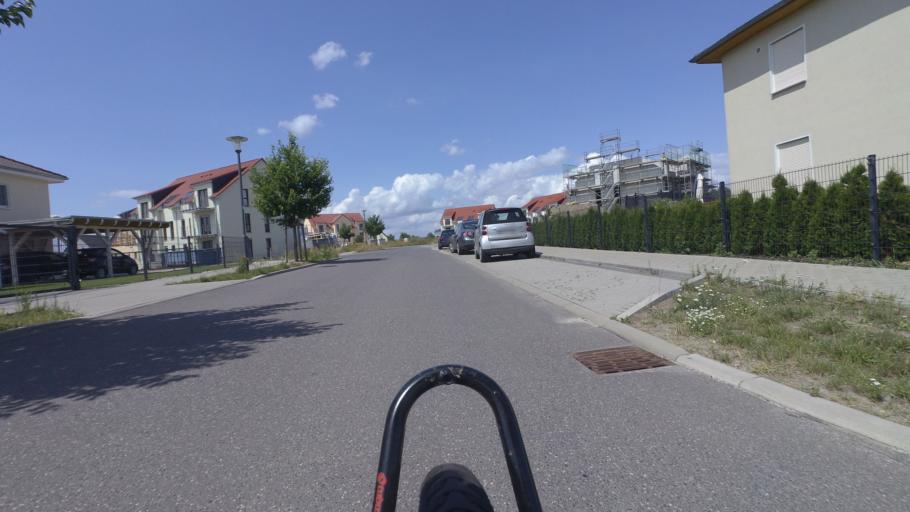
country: DE
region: Brandenburg
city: Grossbeeren
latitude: 52.3483
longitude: 13.3016
